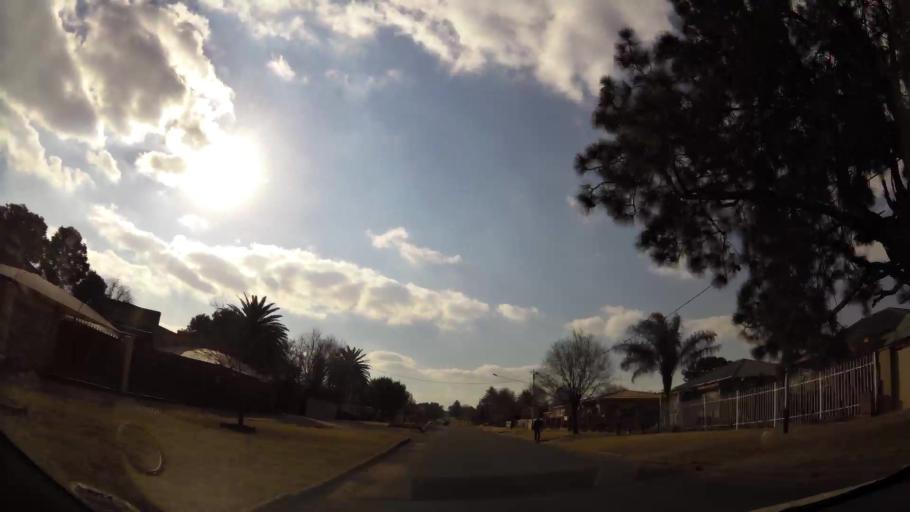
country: ZA
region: Gauteng
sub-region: West Rand District Municipality
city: Krugersdorp
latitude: -26.0898
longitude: 27.7658
